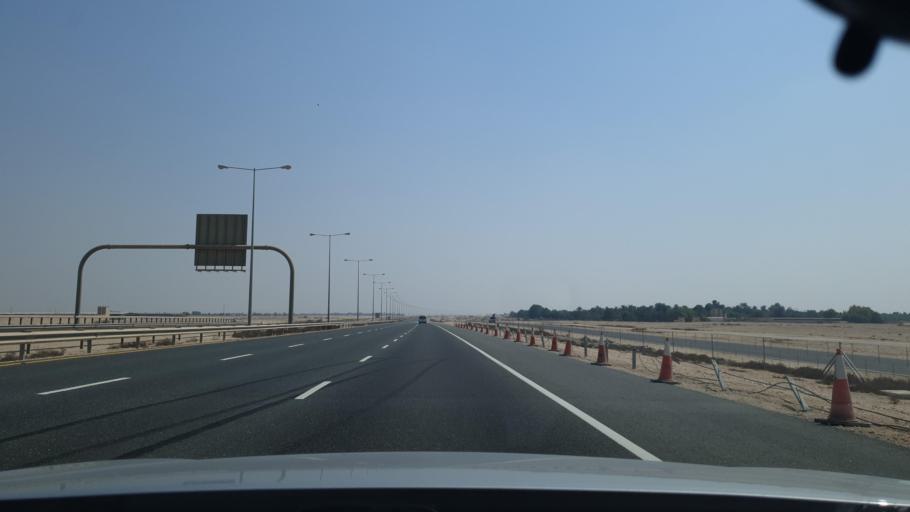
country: QA
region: Al Khawr
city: Al Khawr
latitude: 25.7832
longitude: 51.3995
